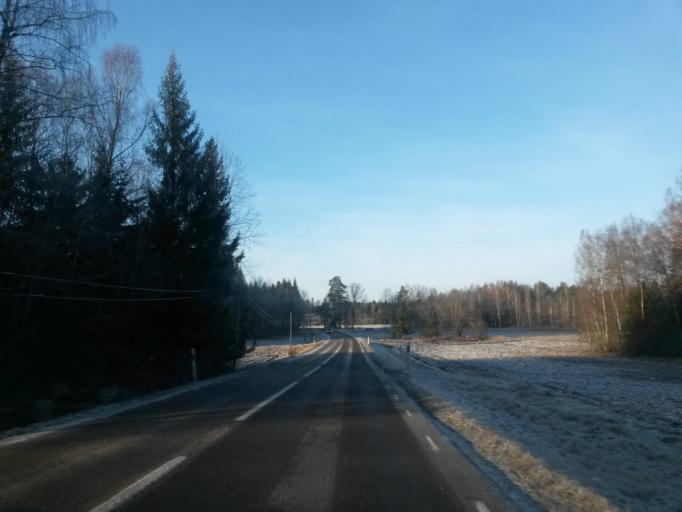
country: SE
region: Vaestra Goetaland
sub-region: Alingsas Kommun
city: Sollebrunn
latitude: 58.1323
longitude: 12.4857
